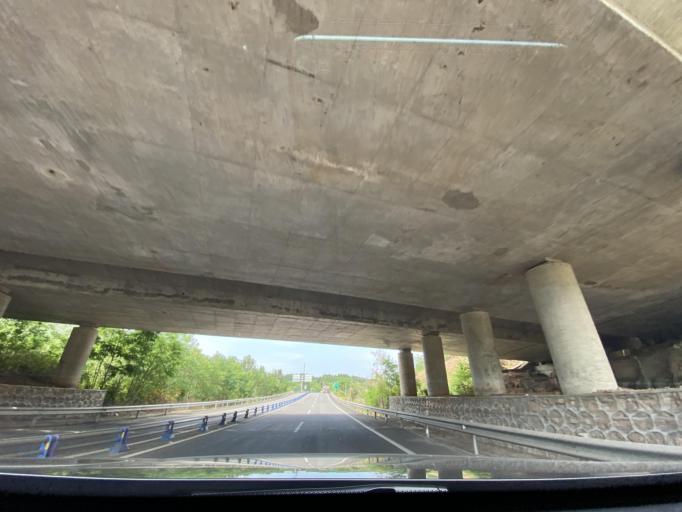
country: CN
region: Sichuan
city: Mianyang
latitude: 31.3502
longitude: 104.7084
